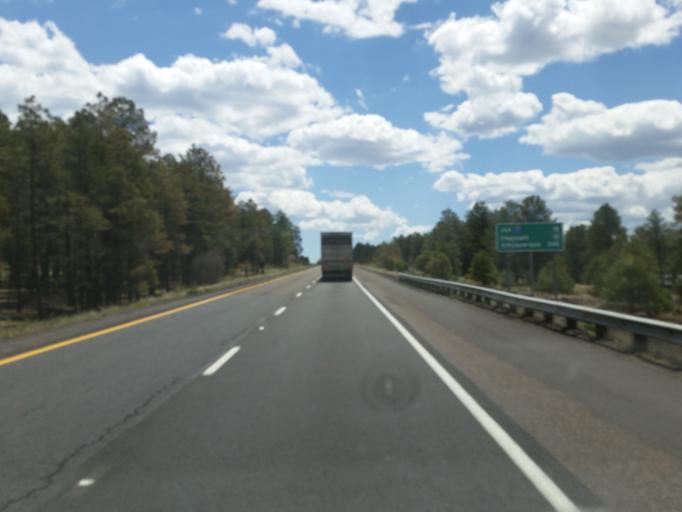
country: US
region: Arizona
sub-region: Coconino County
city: Parks
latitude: 35.2542
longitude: -111.9164
